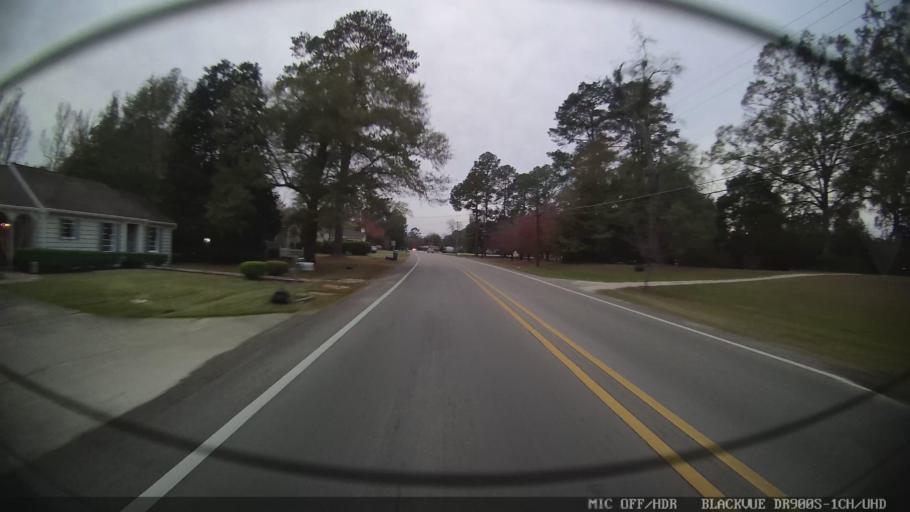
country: US
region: Mississippi
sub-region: Clarke County
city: Quitman
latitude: 32.0387
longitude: -88.7170
